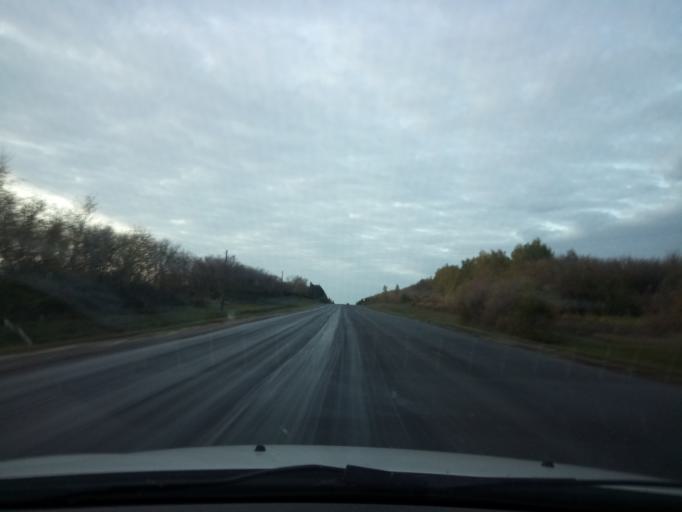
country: RU
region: Nizjnij Novgorod
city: Bol'shoye Murashkino
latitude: 55.8077
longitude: 44.7616
